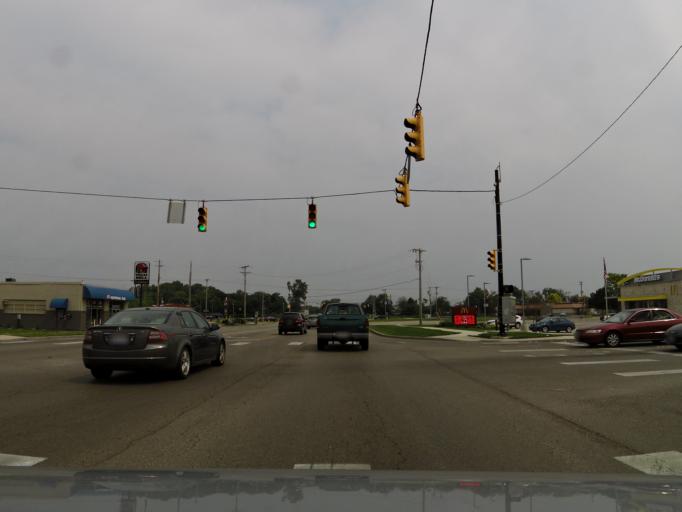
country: US
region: Ohio
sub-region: Montgomery County
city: Riverside
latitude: 39.7676
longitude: -84.1233
